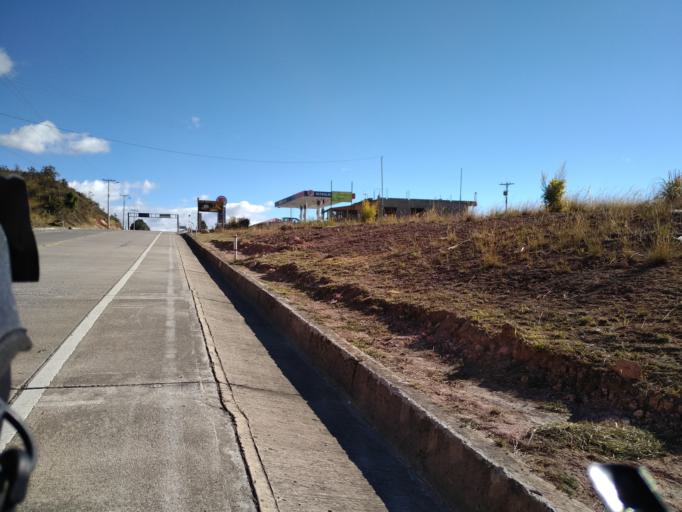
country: EC
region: Azuay
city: Cuenca
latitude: -3.3162
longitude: -79.1530
